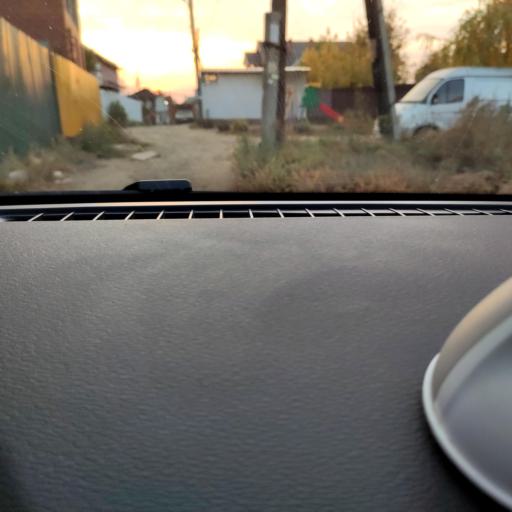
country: RU
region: Samara
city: Samara
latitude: 53.1833
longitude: 50.1210
